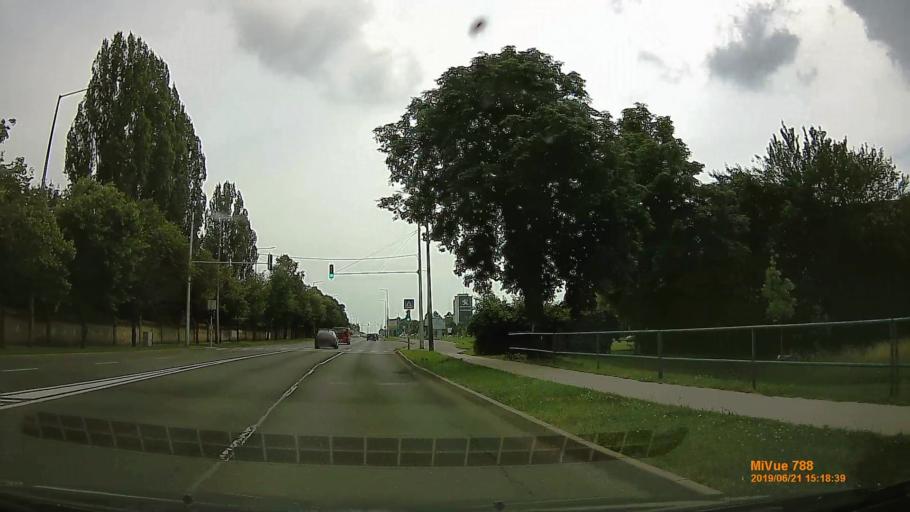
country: HU
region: Baranya
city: Pecs
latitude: 46.0481
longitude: 18.2315
